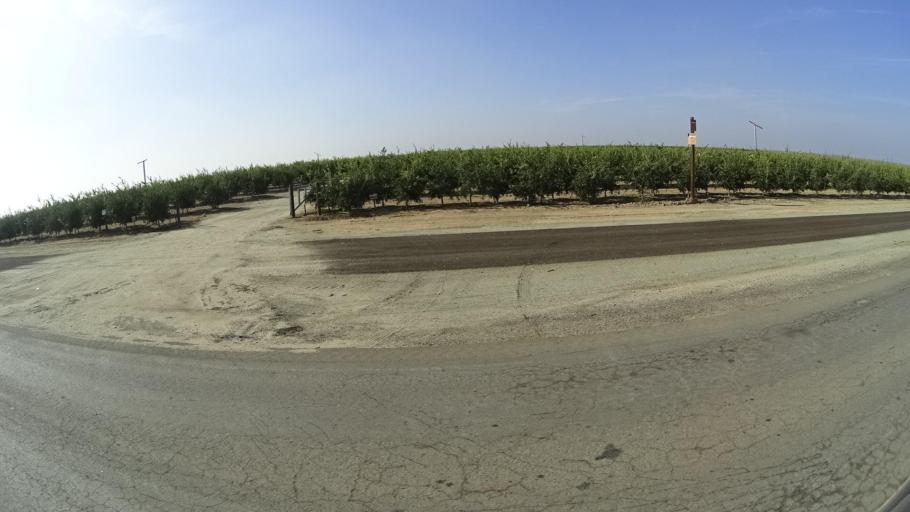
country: US
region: California
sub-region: Kern County
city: McFarland
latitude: 35.6276
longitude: -119.1688
